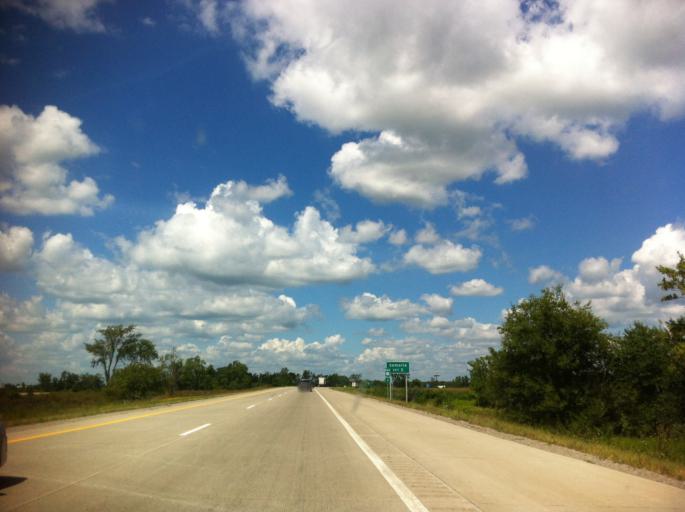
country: US
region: Ohio
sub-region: Lucas County
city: Sylvania
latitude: 41.7830
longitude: -83.6956
